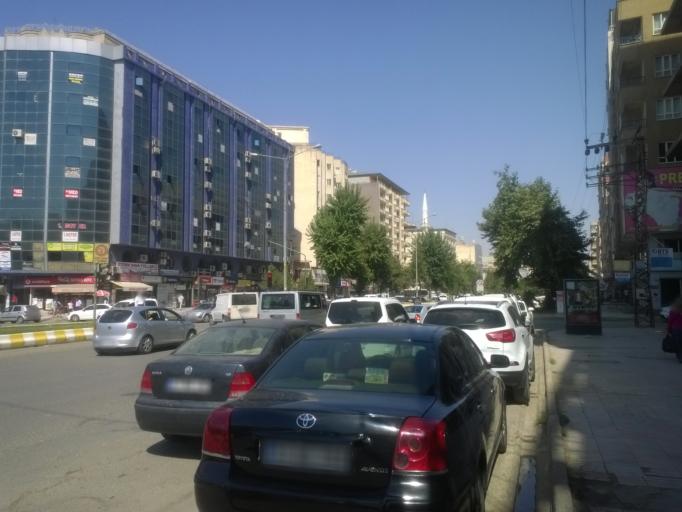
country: TR
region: Batman
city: Batman
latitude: 37.8837
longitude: 41.1277
